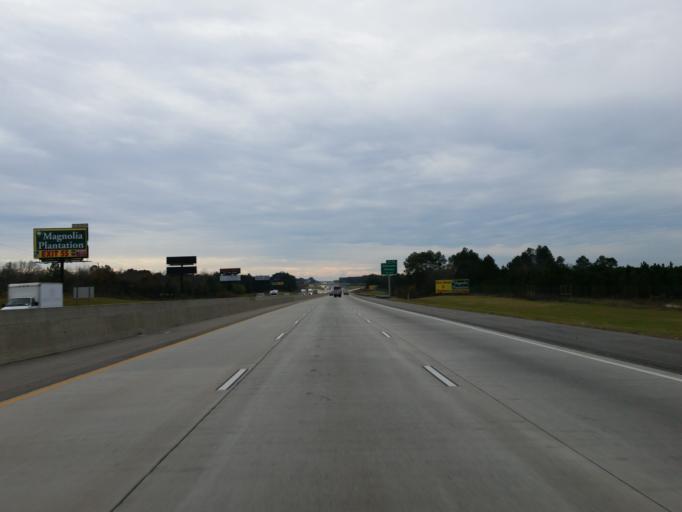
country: US
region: Georgia
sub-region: Tift County
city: Unionville
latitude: 31.3729
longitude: -83.4938
